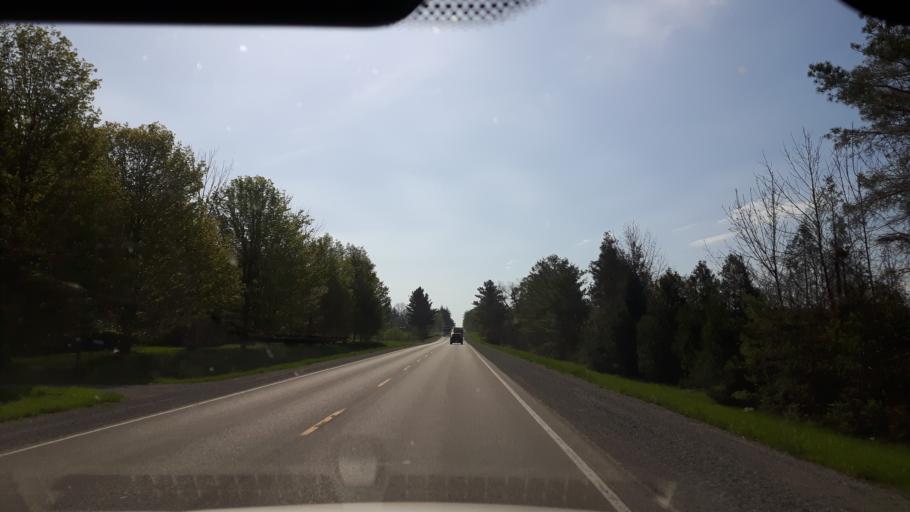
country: CA
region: Ontario
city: Bluewater
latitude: 43.5534
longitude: -81.6772
